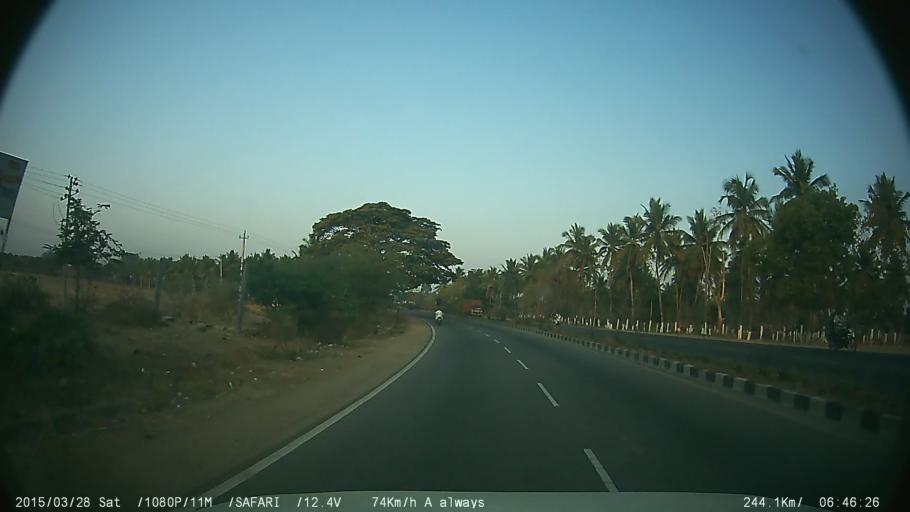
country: IN
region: Karnataka
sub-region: Mandya
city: Maddur
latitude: 12.6174
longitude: 77.0867
